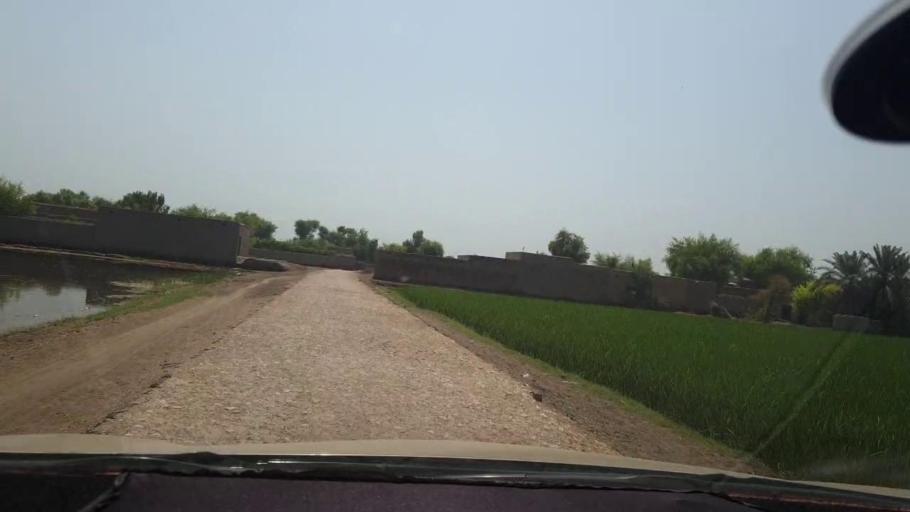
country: PK
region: Sindh
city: Kambar
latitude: 27.6353
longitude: 67.9332
